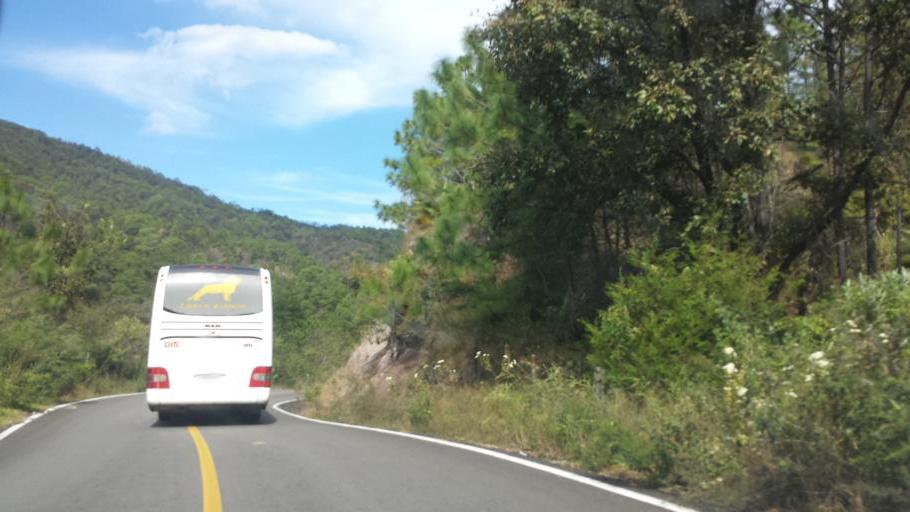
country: MX
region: Oaxaca
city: San Francisco Sola
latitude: 16.4531
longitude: -97.0318
